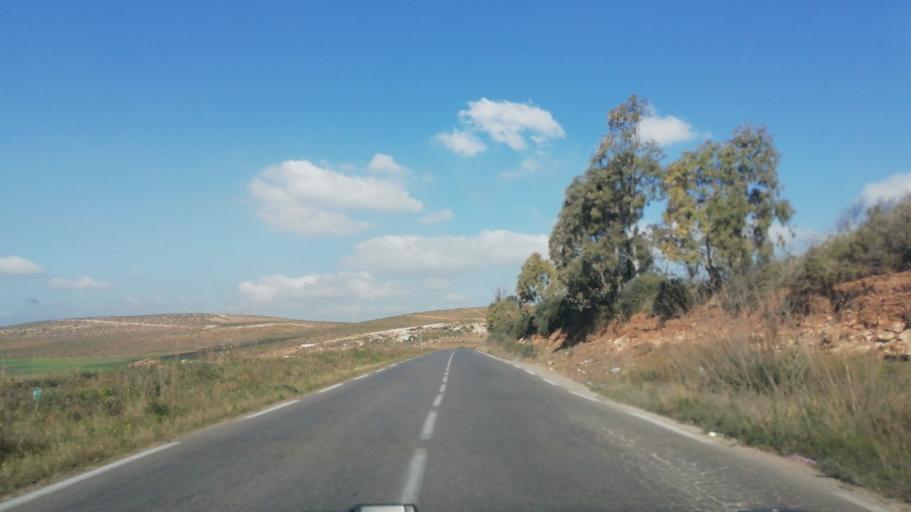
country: DZ
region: Oran
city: Ain el Bya
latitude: 35.7414
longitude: -0.2582
